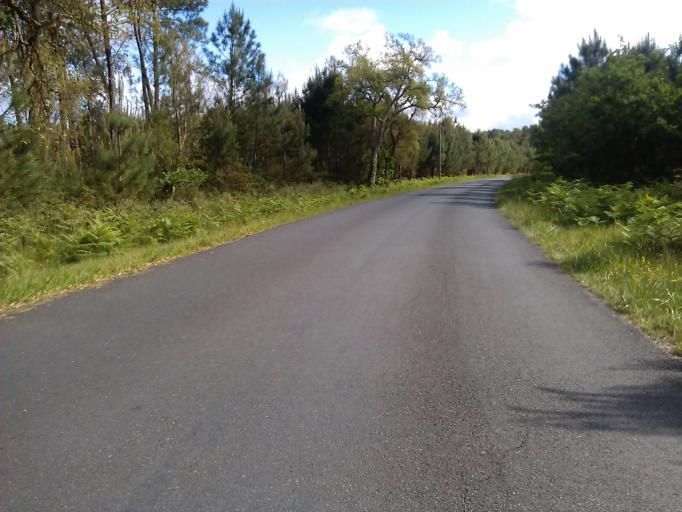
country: FR
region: Aquitaine
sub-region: Departement des Landes
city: Leon
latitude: 43.8623
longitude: -1.3570
